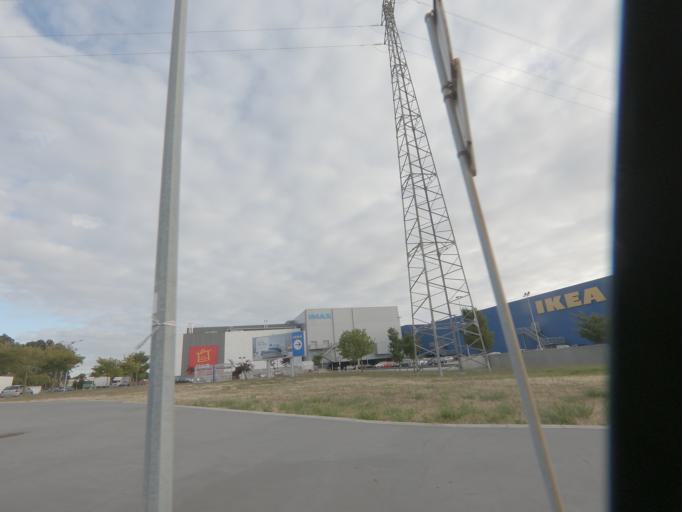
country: PT
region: Porto
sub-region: Matosinhos
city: Santa Cruz do Bispo
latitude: 41.2111
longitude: -8.6862
